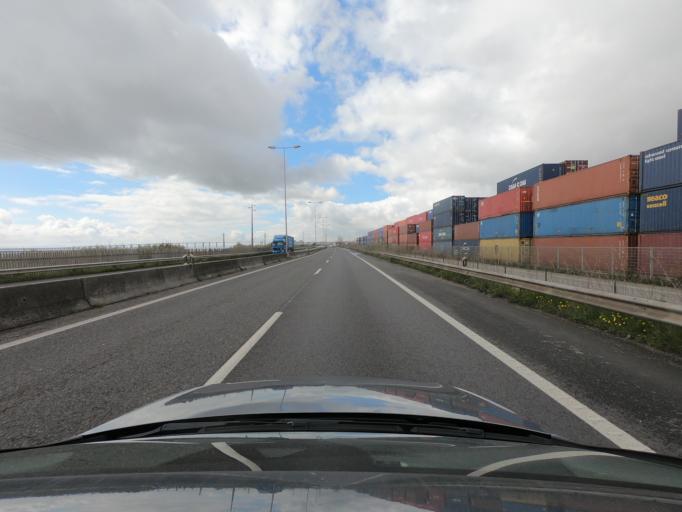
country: PT
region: Lisbon
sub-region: Loures
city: Sao Joao da Talha
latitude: 38.8195
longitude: -9.0863
